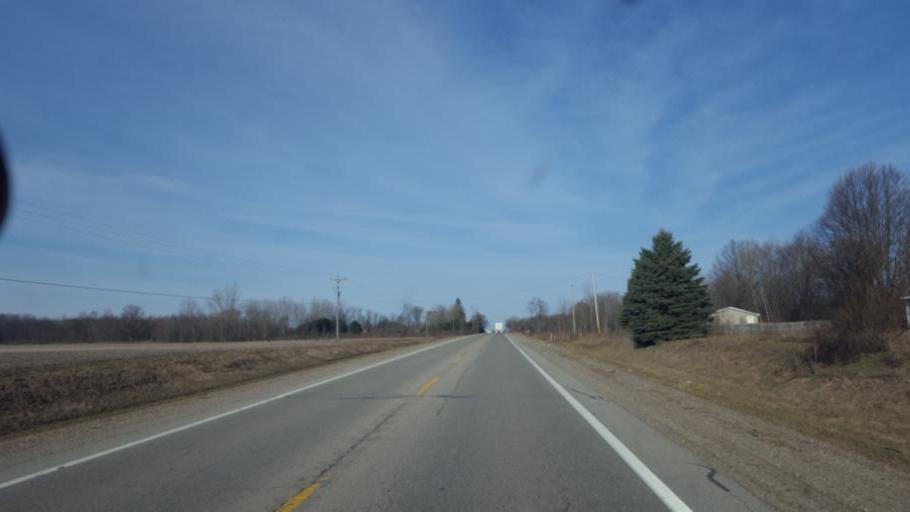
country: US
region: Michigan
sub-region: Montcalm County
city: Lakeview
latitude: 43.4301
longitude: -85.1740
